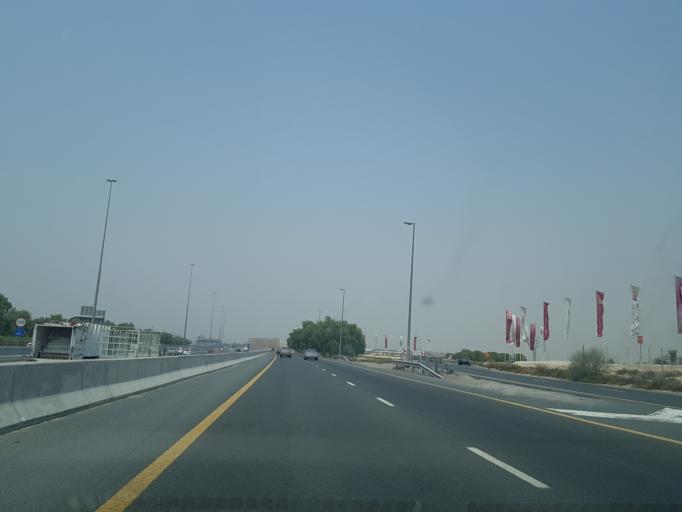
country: AE
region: Dubai
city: Dubai
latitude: 25.1272
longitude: 55.3744
